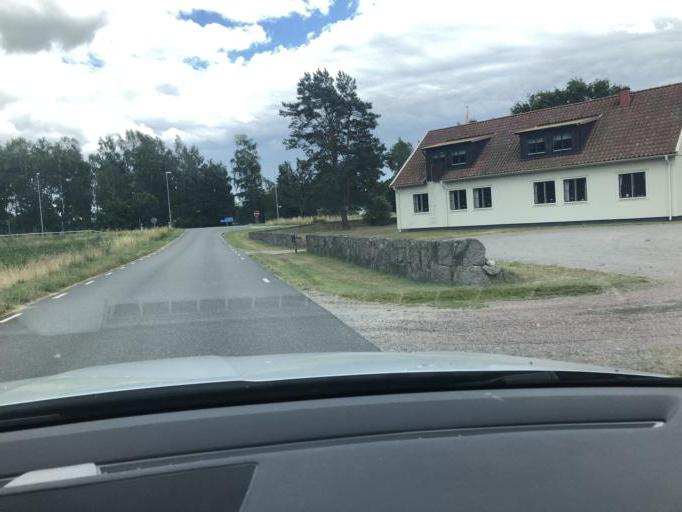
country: SE
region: Blekinge
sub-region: Solvesborgs Kommun
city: Soelvesborg
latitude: 56.0913
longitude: 14.6494
